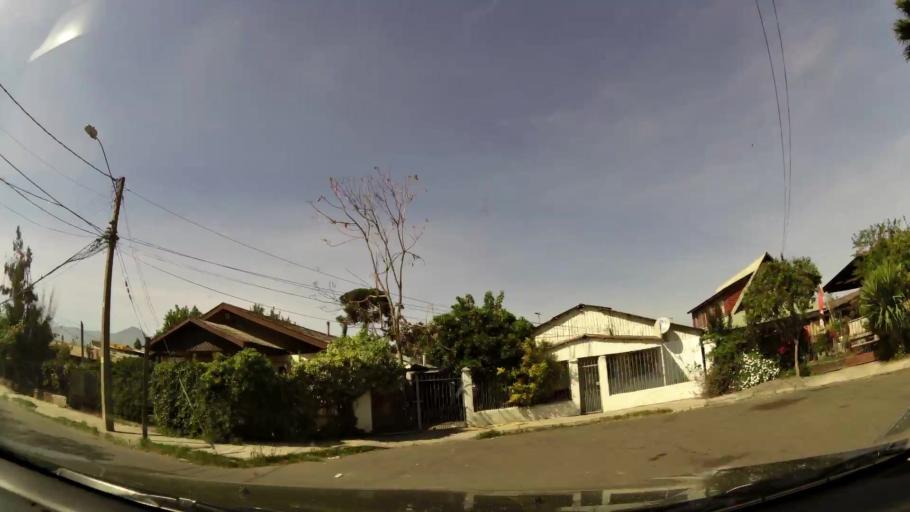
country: CL
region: Santiago Metropolitan
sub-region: Provincia de Cordillera
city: Puente Alto
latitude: -33.6124
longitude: -70.5847
